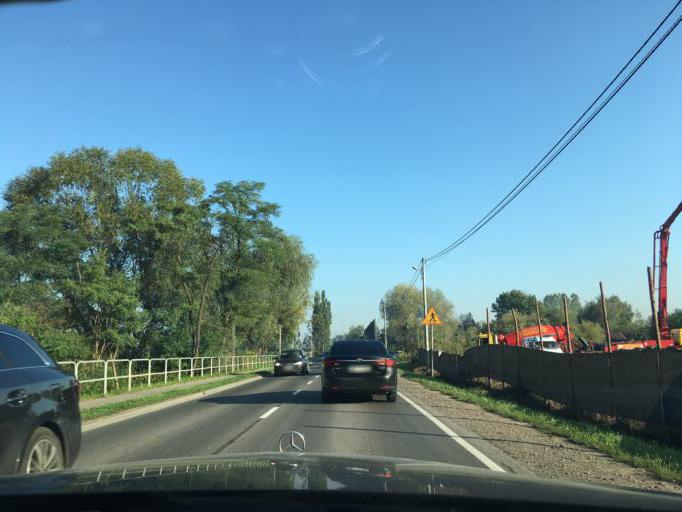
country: PL
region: Masovian Voivodeship
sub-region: Powiat grodziski
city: Grodzisk Mazowiecki
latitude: 52.1402
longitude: 20.6166
